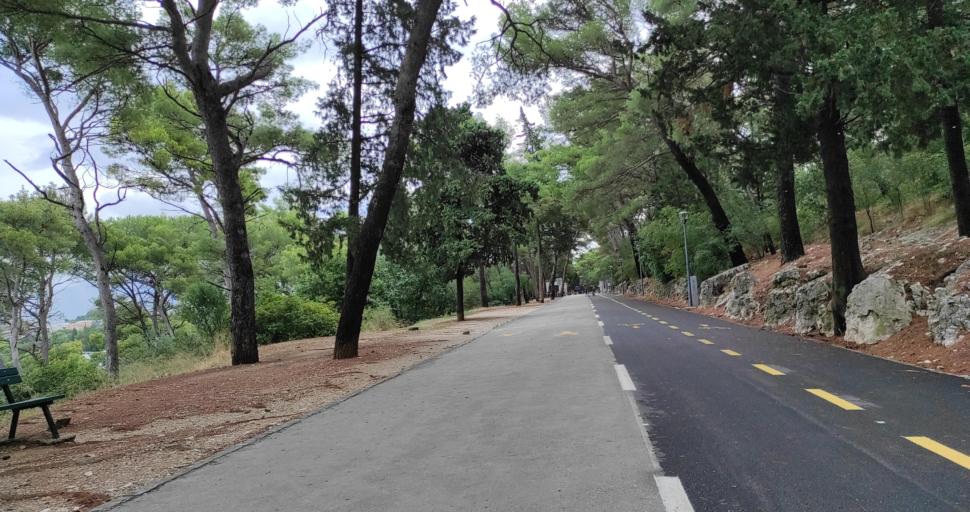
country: HR
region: Splitsko-Dalmatinska
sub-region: Grad Split
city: Split
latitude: 43.5139
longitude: 16.4191
